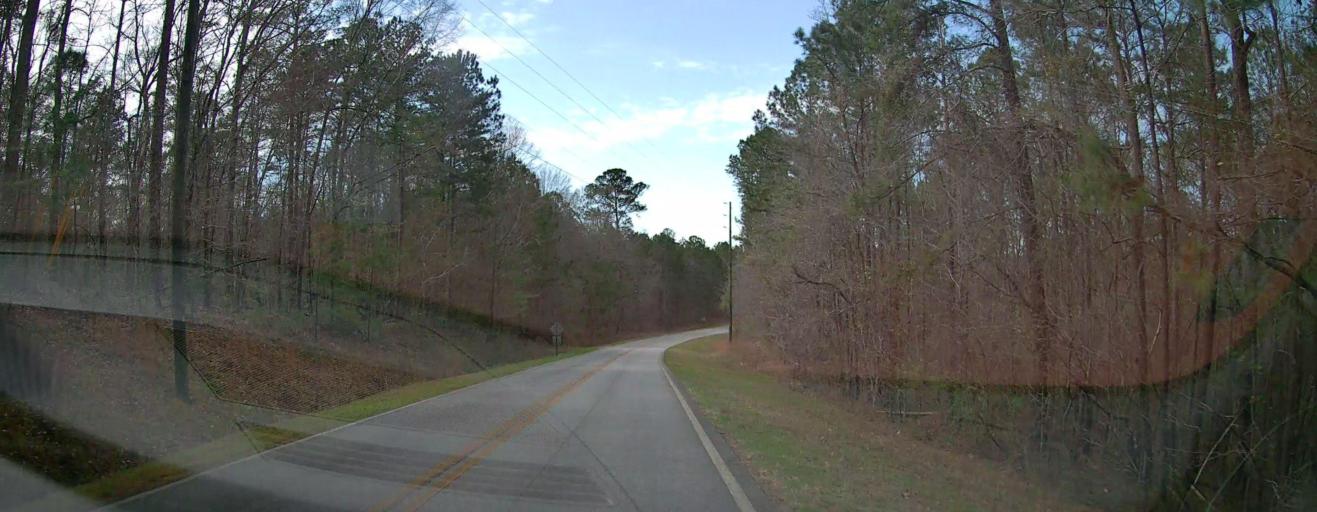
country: US
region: Georgia
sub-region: Jones County
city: Gray
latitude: 33.0541
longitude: -83.7223
